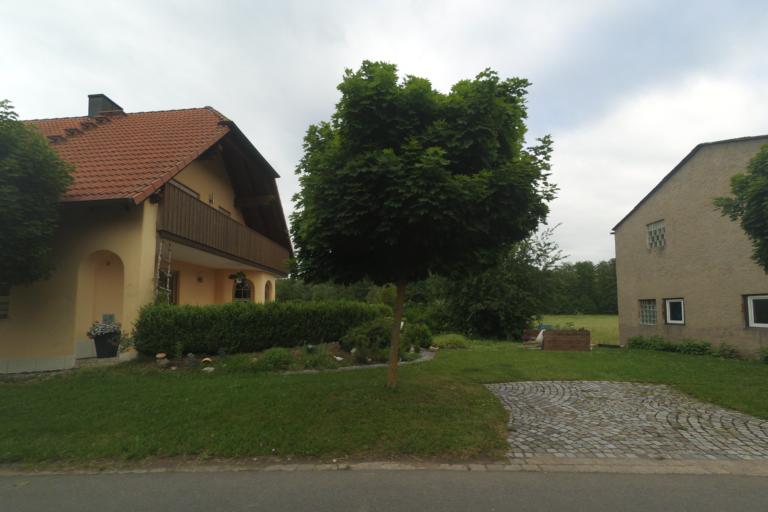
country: DE
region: Bavaria
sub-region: Regierungsbezirk Mittelfranken
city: Burghaslach
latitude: 49.7277
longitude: 10.5987
